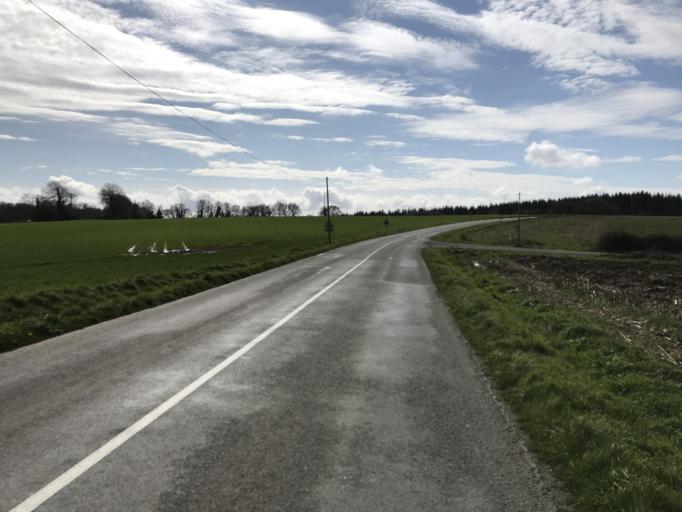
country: FR
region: Brittany
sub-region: Departement du Finistere
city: Dirinon
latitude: 48.3817
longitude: -4.2675
